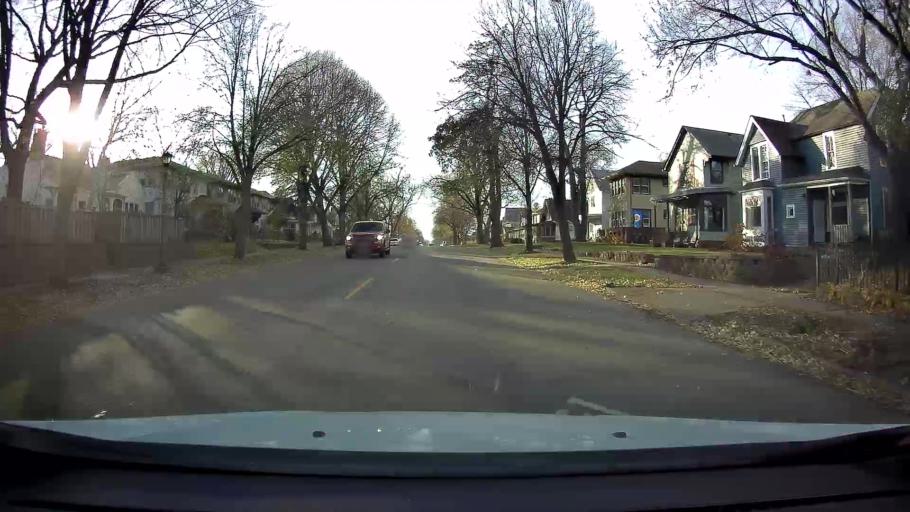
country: US
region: Minnesota
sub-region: Dakota County
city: West Saint Paul
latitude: 44.9342
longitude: -93.1431
